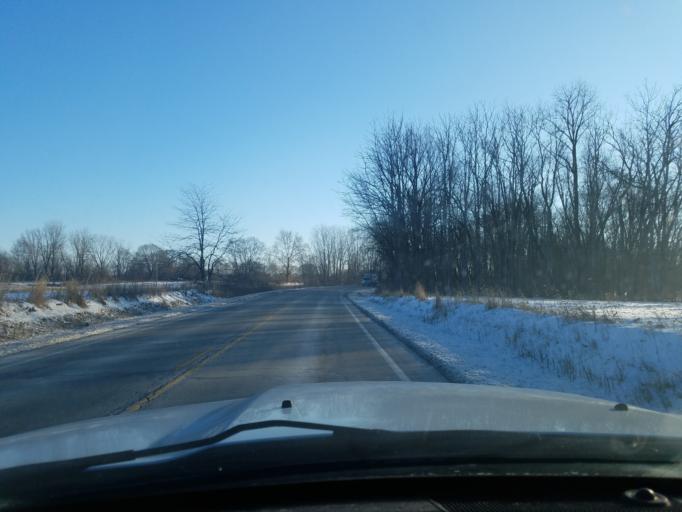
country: US
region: Indiana
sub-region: Noble County
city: Ligonier
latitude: 41.4593
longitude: -85.5159
